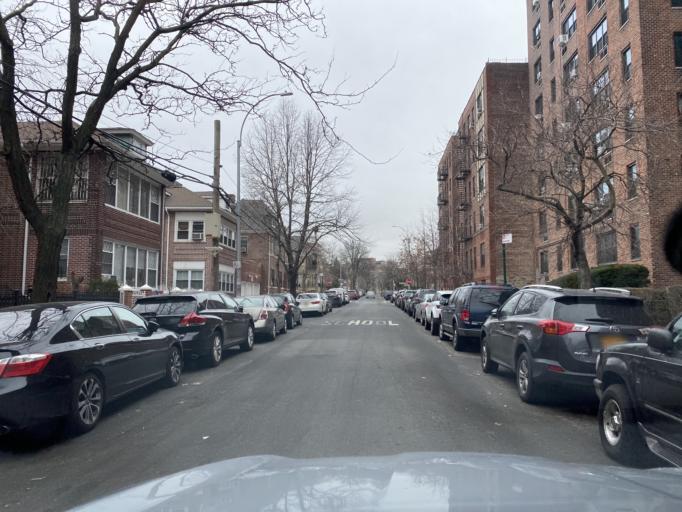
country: US
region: New York
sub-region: New York County
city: Inwood
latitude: 40.8730
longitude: -73.9008
